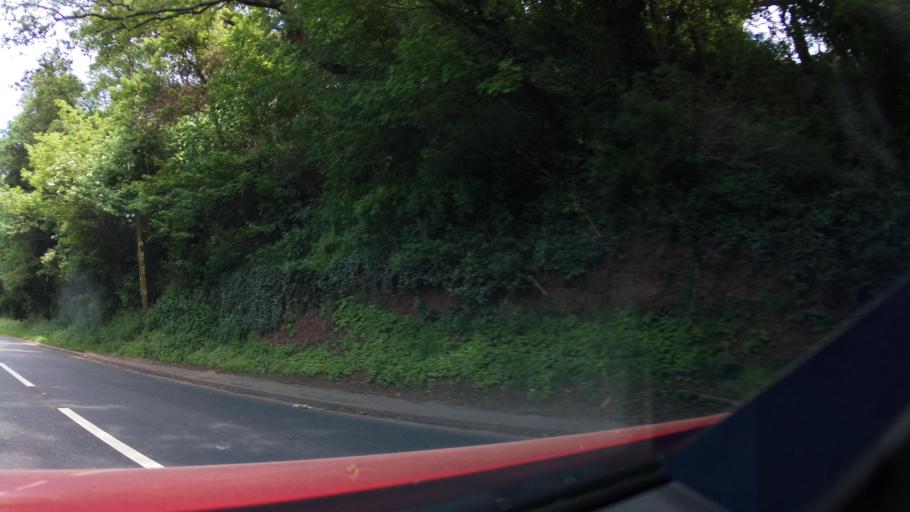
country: GB
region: England
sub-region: Worcestershire
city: Bransford
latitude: 52.1796
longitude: -2.2814
